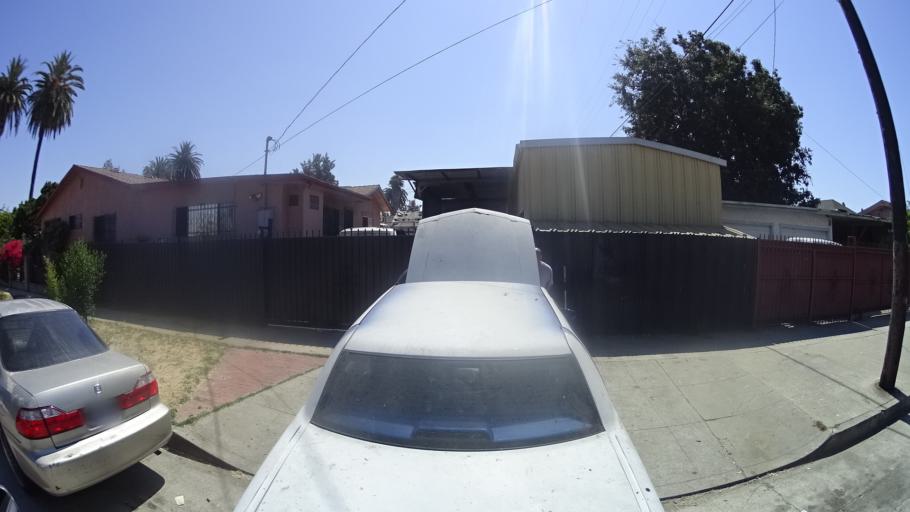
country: US
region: California
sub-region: Los Angeles County
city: Westmont
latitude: 33.9767
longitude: -118.2959
